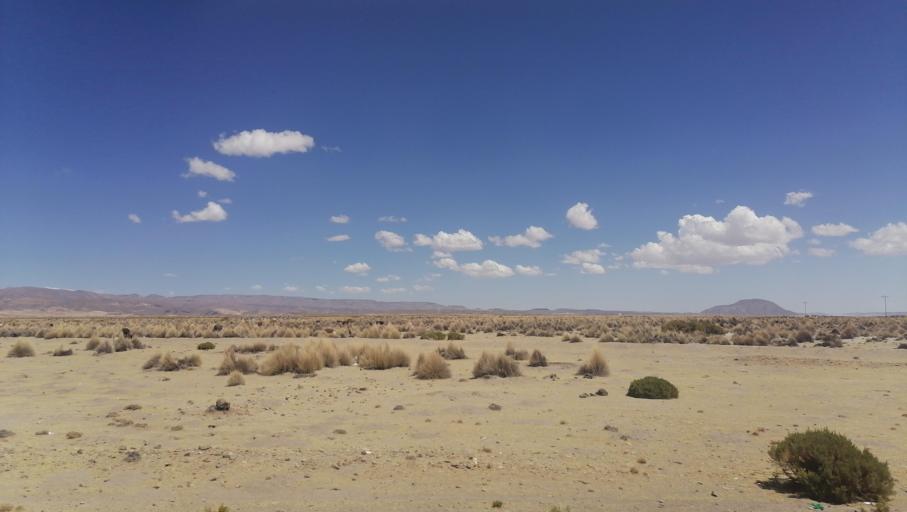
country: BO
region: Oruro
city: Challapata
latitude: -19.1714
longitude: -66.7941
